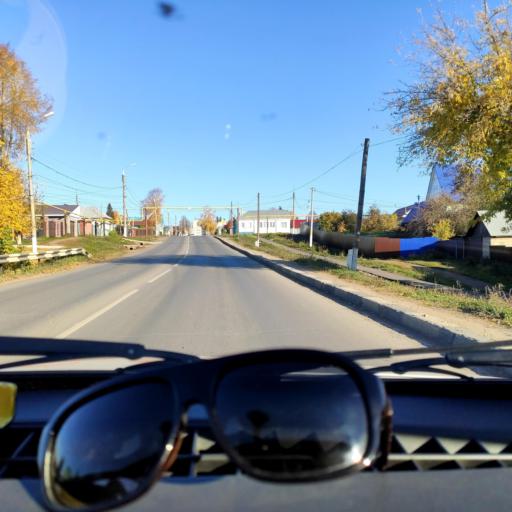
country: RU
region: Bashkortostan
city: Blagoveshchensk
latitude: 55.0414
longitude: 55.9614
